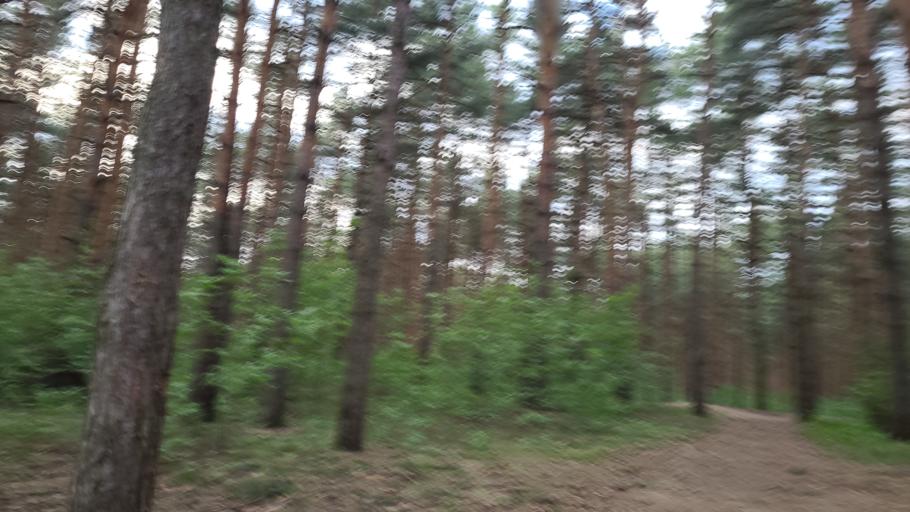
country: RU
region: Moskovskaya
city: Kratovo
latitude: 55.5567
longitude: 38.1820
